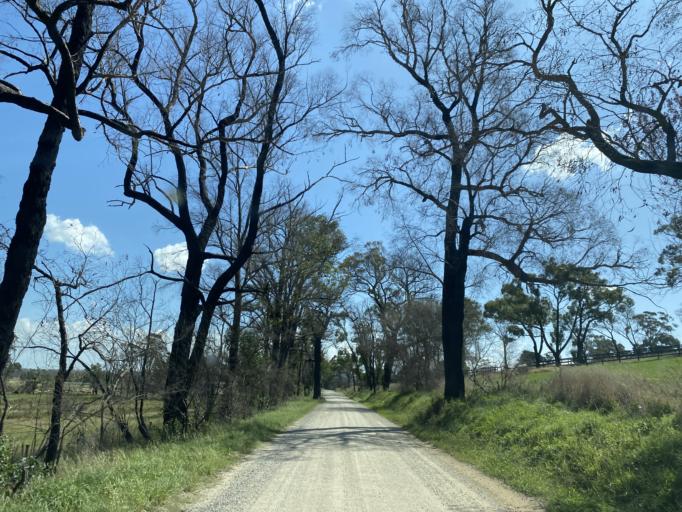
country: AU
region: Victoria
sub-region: Cardinia
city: Bunyip
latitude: -38.0390
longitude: 145.7426
